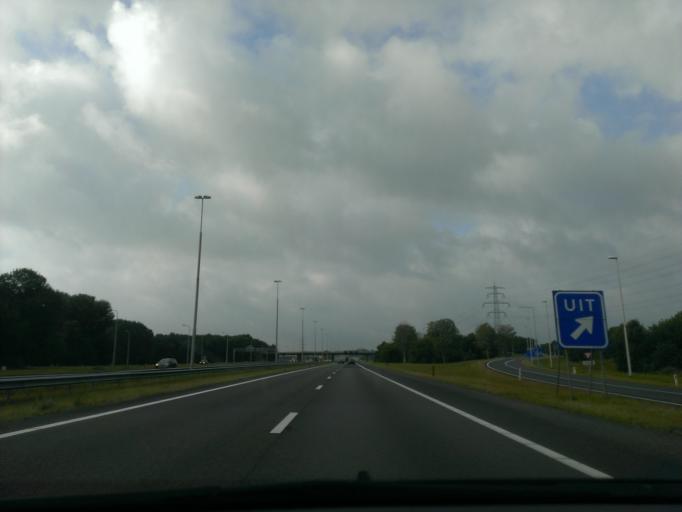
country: NL
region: Gelderland
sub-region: Gemeente Apeldoorn
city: Apeldoorn
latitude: 52.2107
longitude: 6.0222
